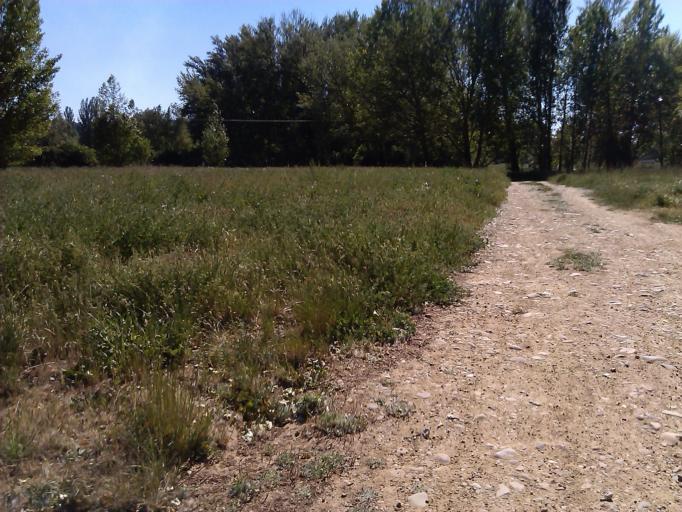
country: ES
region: Castille and Leon
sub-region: Provincia de Burgos
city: Cardenajimeno
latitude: 42.3411
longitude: -3.6370
